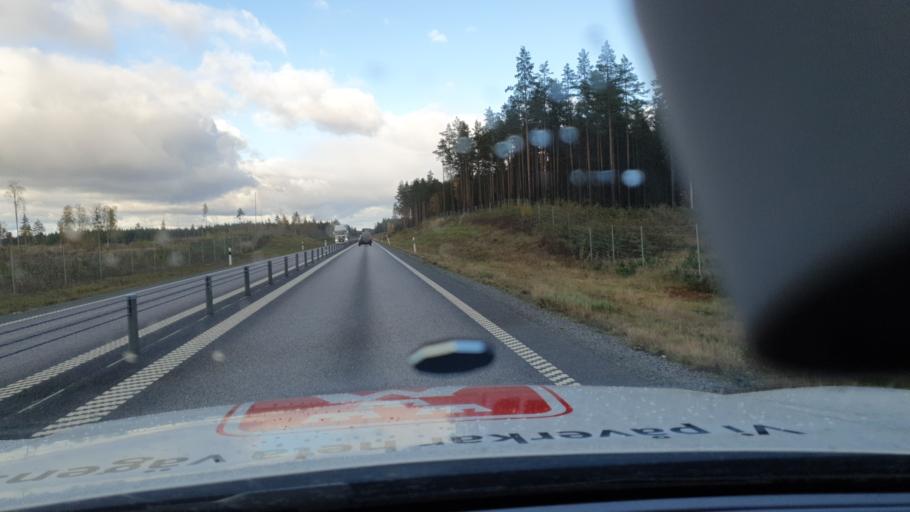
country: SE
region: Uppsala
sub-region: Heby Kommun
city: Tarnsjo
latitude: 60.0952
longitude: 16.9195
